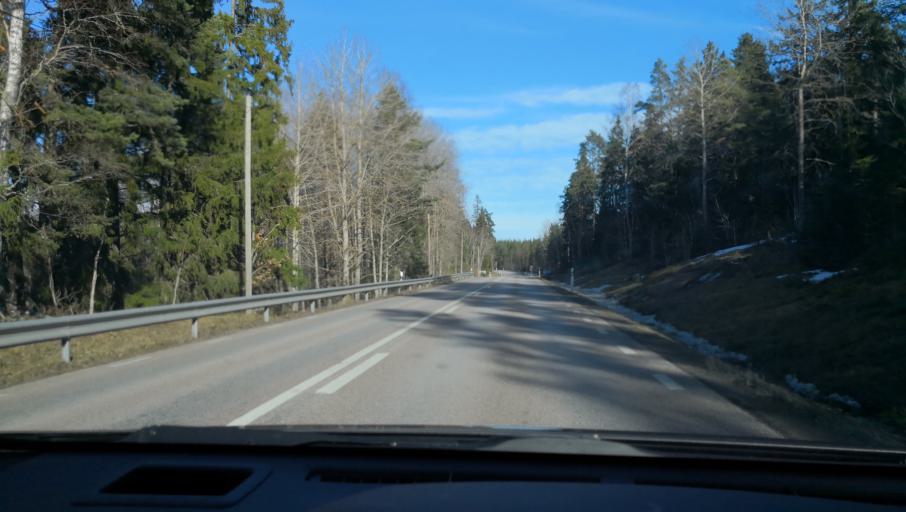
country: SE
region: Uppsala
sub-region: Osthammars Kommun
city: Osterbybruk
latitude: 60.1443
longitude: 17.8224
